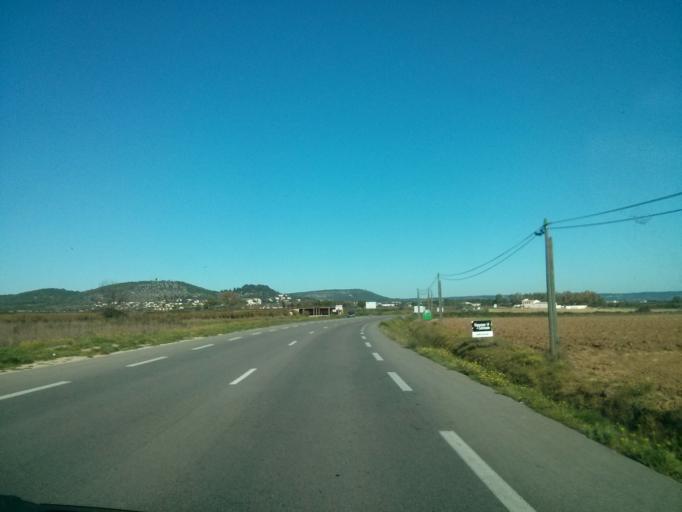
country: FR
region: Languedoc-Roussillon
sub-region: Departement du Gard
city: Calvisson
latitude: 43.7635
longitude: 4.2017
